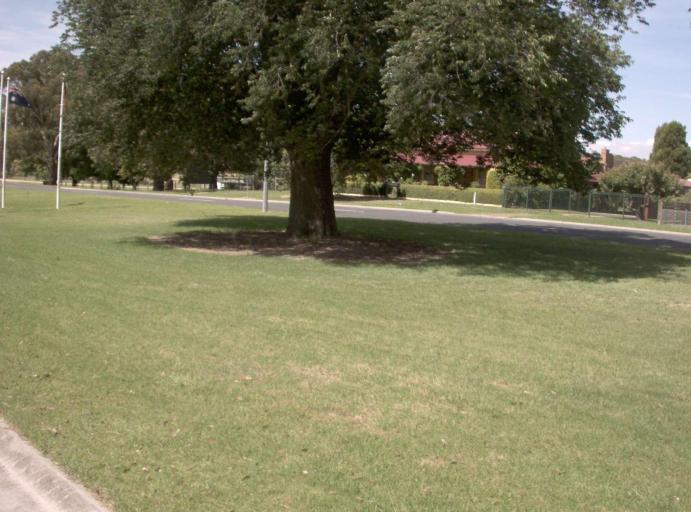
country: AU
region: Victoria
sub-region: Wellington
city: Heyfield
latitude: -38.1500
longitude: 146.7897
